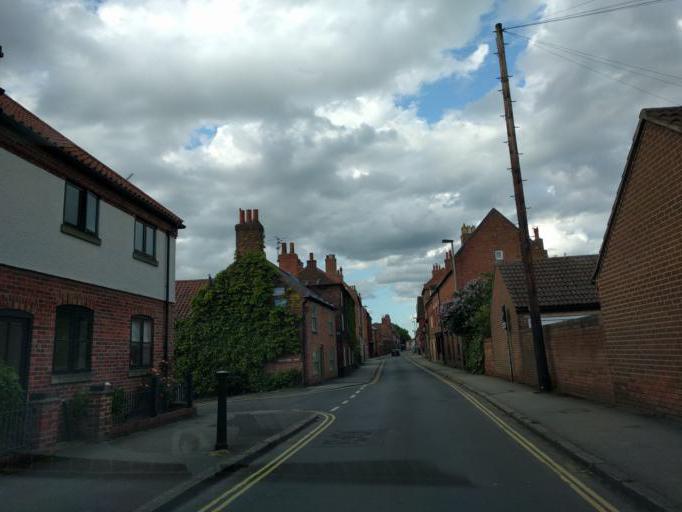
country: GB
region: England
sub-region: Nottinghamshire
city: Newark on Trent
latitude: 53.0748
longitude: -0.8159
